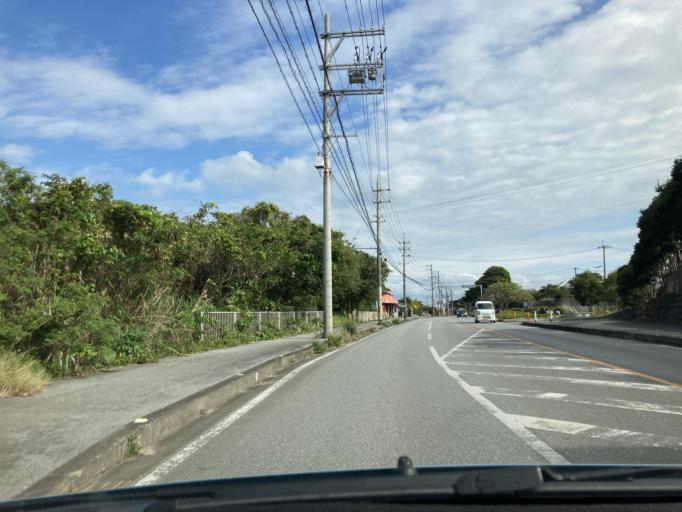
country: JP
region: Okinawa
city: Nago
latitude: 26.6926
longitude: 127.9572
